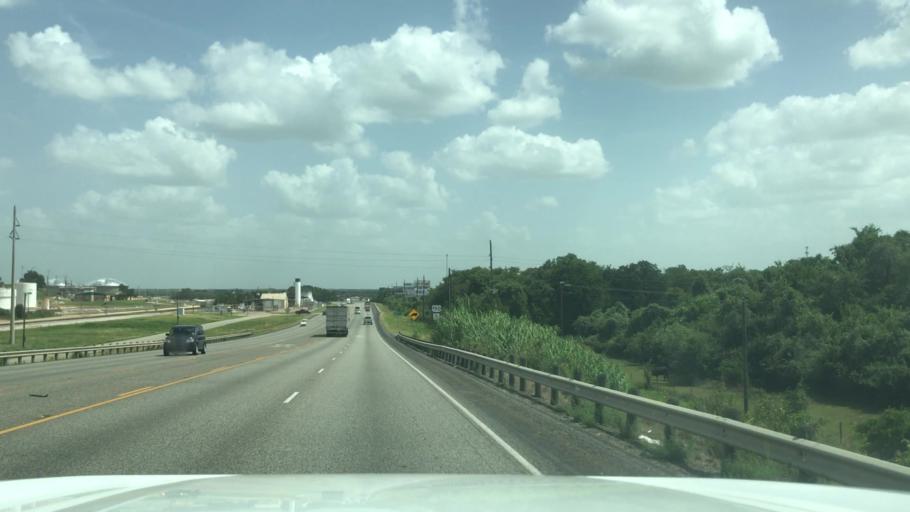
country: US
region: Texas
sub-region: Robertson County
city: Hearne
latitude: 30.8665
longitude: -96.5840
